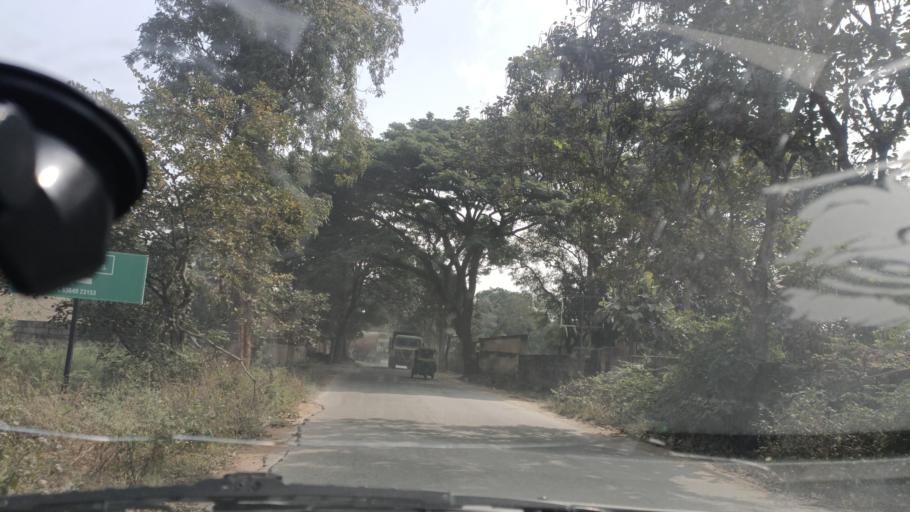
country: IN
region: Karnataka
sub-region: Bangalore Urban
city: Yelahanka
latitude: 13.1598
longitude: 77.6398
